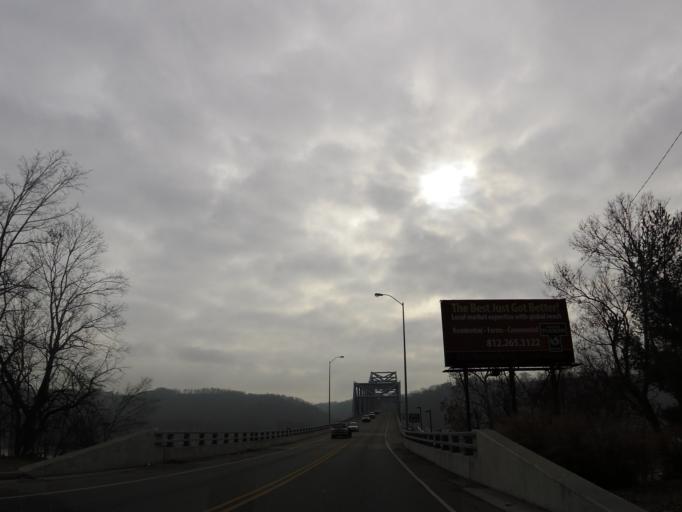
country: US
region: Indiana
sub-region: Jefferson County
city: Madison
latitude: 38.7336
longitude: -85.3698
